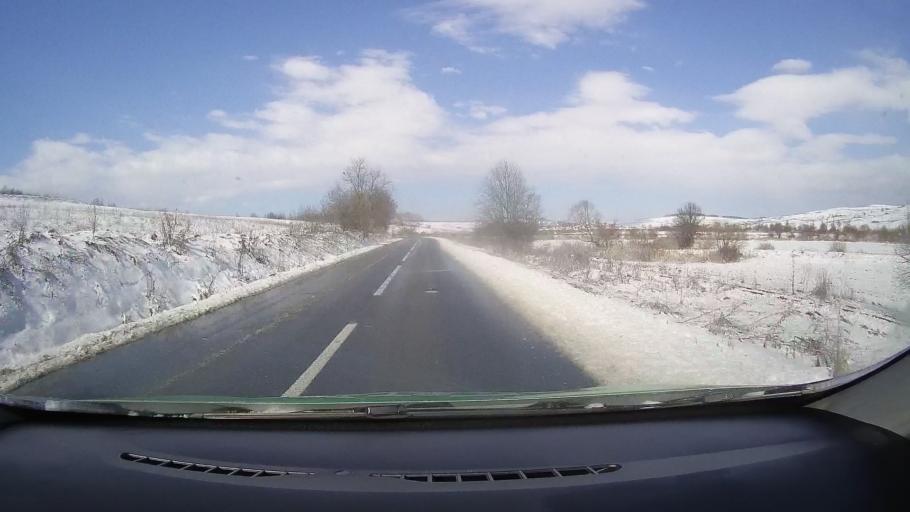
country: RO
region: Sibiu
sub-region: Comuna Nocrich
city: Nocrich
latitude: 45.9068
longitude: 24.4639
